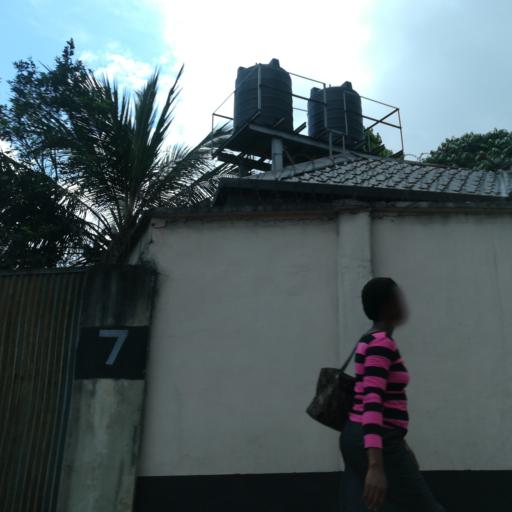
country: NG
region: Rivers
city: Port Harcourt
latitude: 4.8120
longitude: 7.0608
